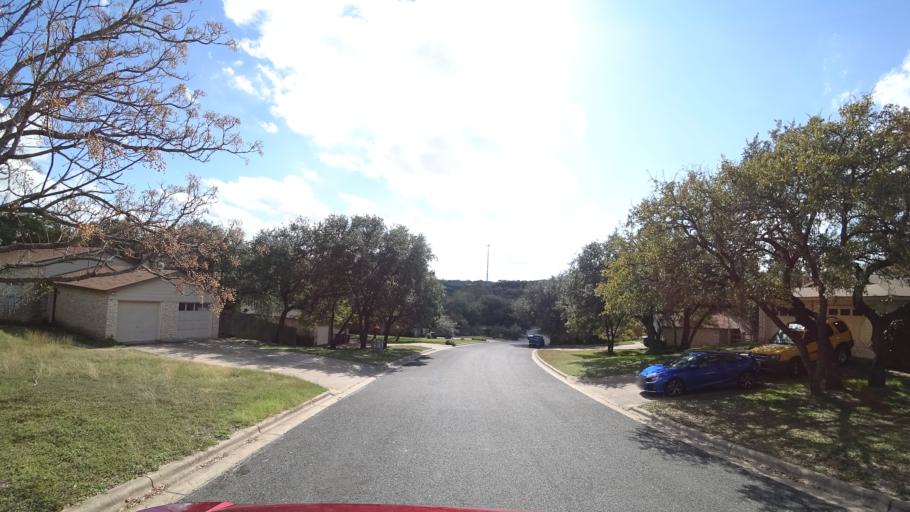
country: US
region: Texas
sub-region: Williamson County
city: Jollyville
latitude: 30.4209
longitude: -97.8003
